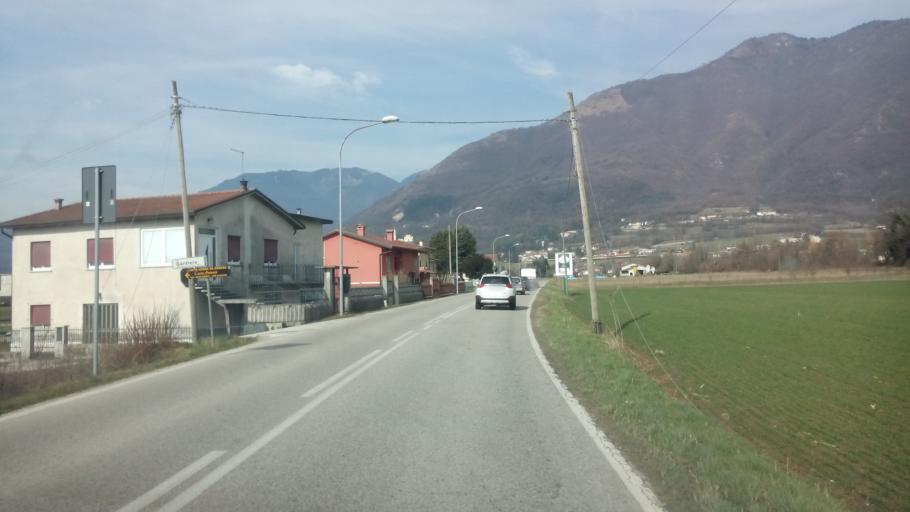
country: IT
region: Veneto
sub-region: Provincia di Vicenza
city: Santorso
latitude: 45.7298
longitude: 11.4135
